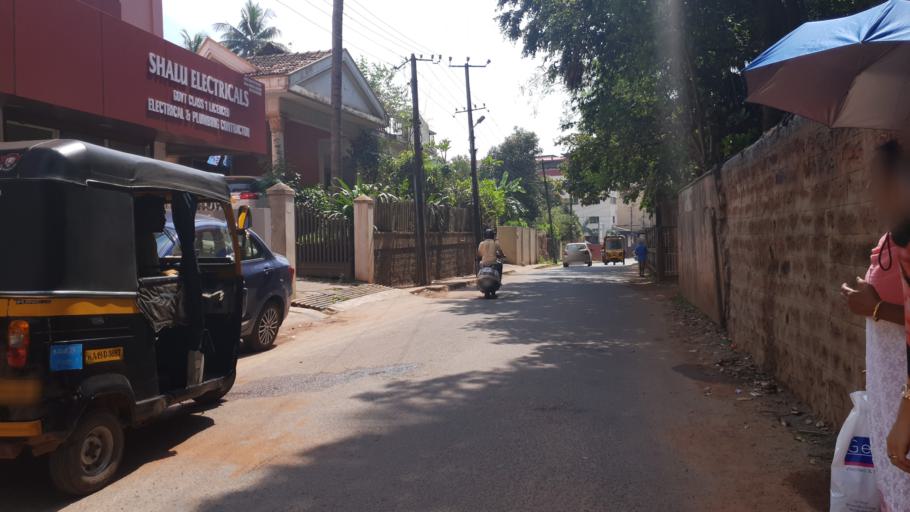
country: IN
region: Karnataka
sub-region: Dakshina Kannada
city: Ullal
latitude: 12.8484
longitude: 74.8461
